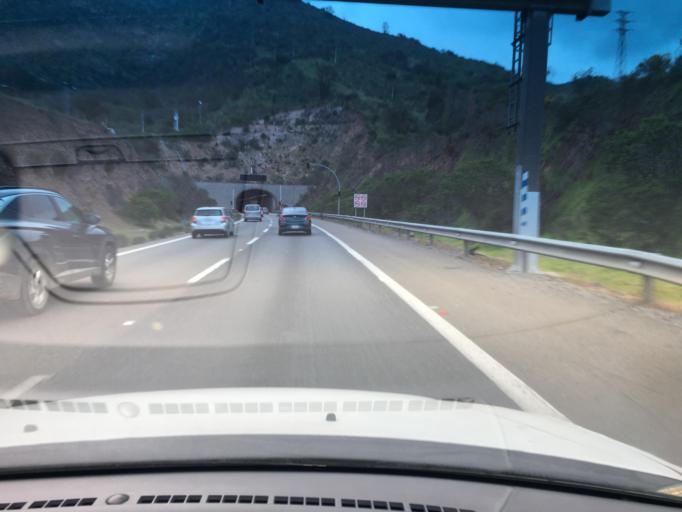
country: CL
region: Santiago Metropolitan
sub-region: Provincia de Talagante
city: Penaflor
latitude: -33.4566
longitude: -70.9323
